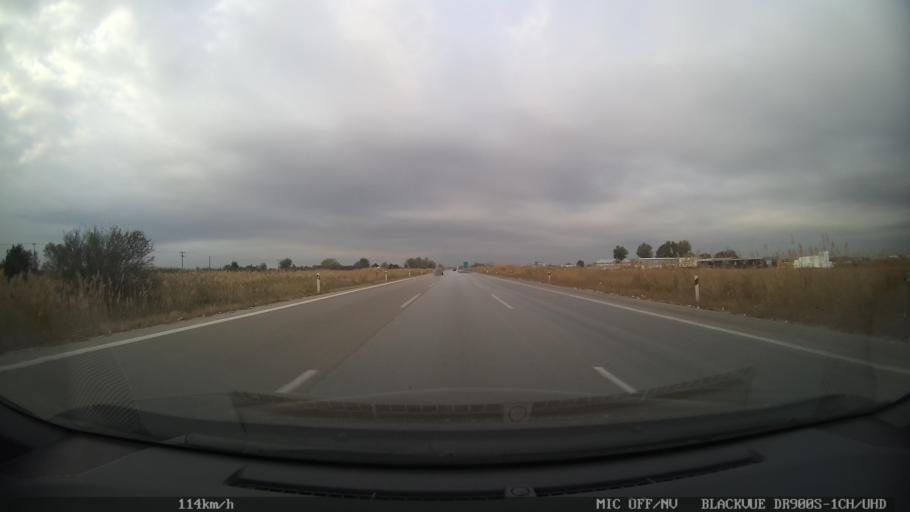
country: GR
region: Central Macedonia
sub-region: Nomos Thessalonikis
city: Chalastra
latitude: 40.6217
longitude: 22.7578
